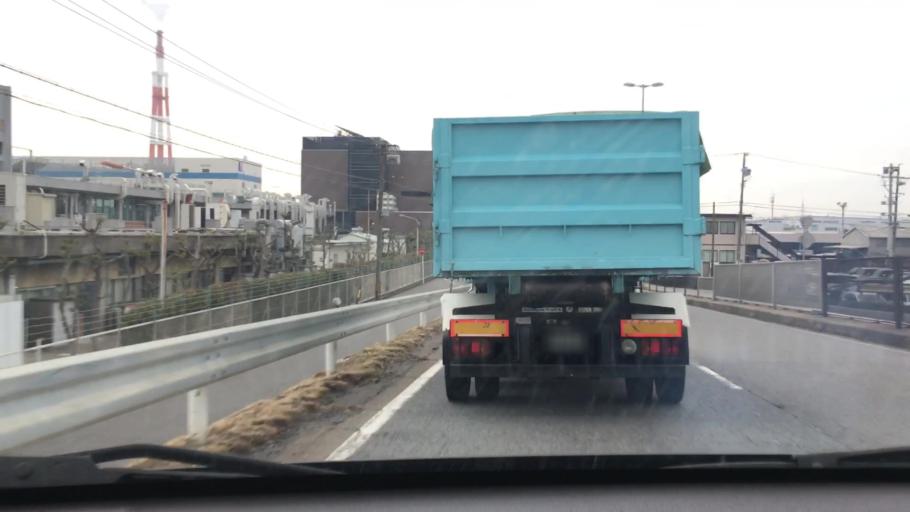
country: JP
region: Mie
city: Yokkaichi
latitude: 34.9308
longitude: 136.6052
